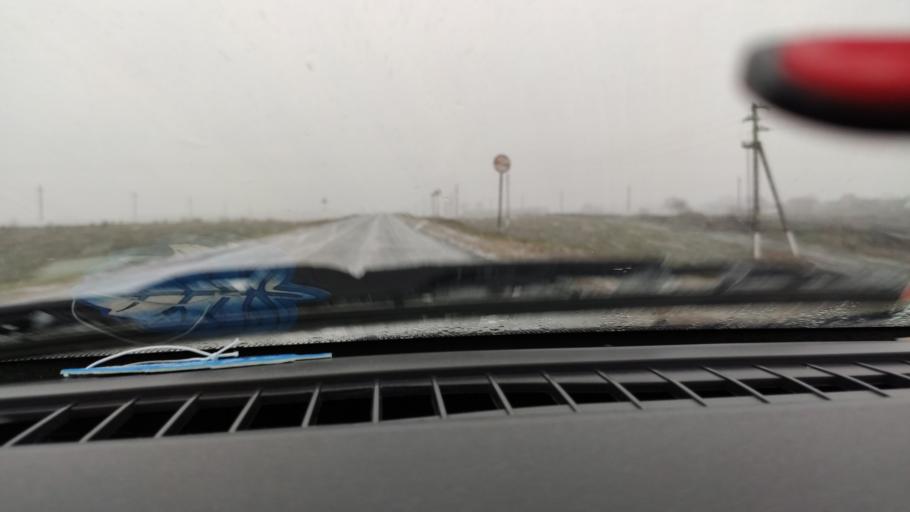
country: RU
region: Tatarstan
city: Cheremshan
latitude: 54.7211
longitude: 51.2576
